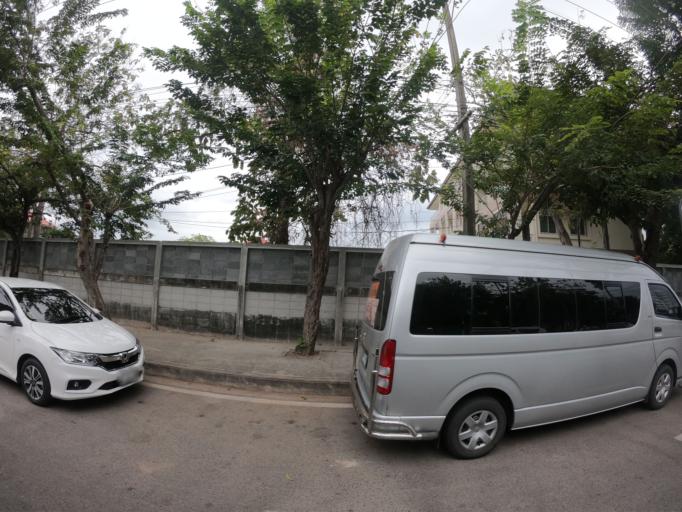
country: TH
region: Roi Et
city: Roi Et
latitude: 16.0511
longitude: 103.6536
